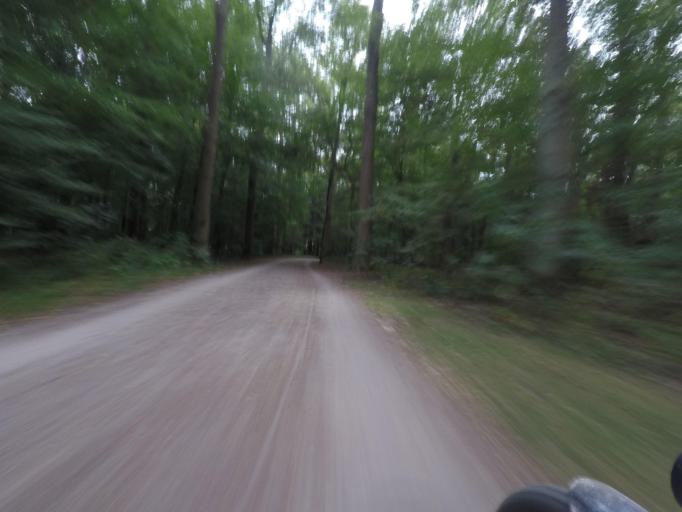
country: DE
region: Hamburg
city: Bergstedt
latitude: 53.6418
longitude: 10.1432
